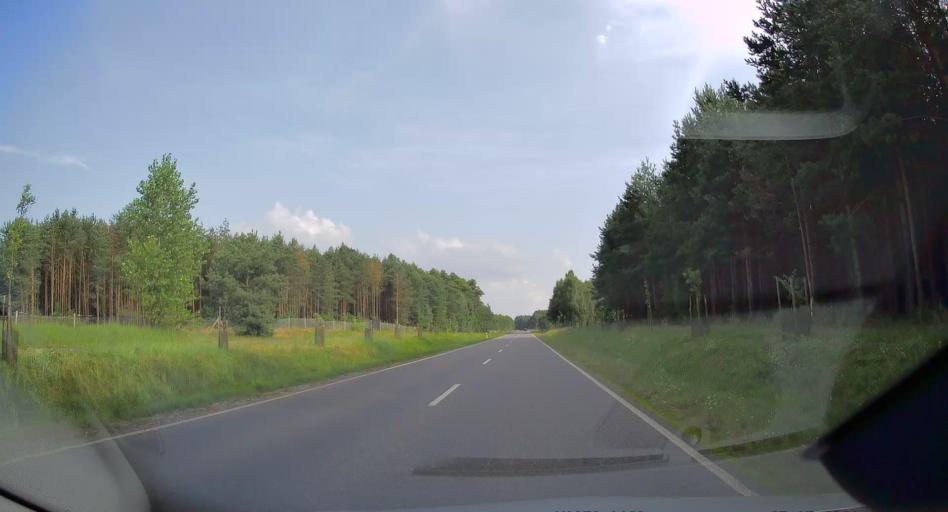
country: PL
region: Lodz Voivodeship
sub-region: Powiat tomaszowski
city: Inowlodz
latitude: 51.4620
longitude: 20.2588
